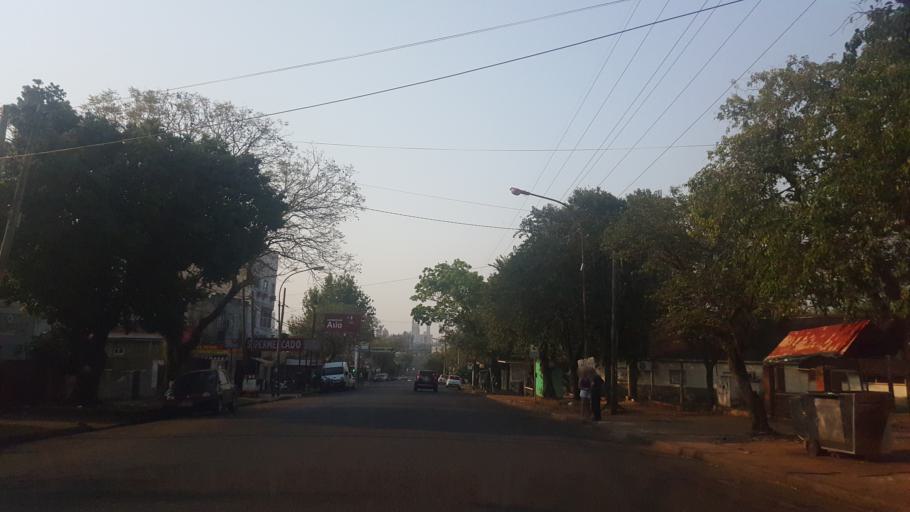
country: AR
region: Misiones
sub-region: Departamento de Capital
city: Posadas
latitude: -27.3843
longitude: -55.8923
